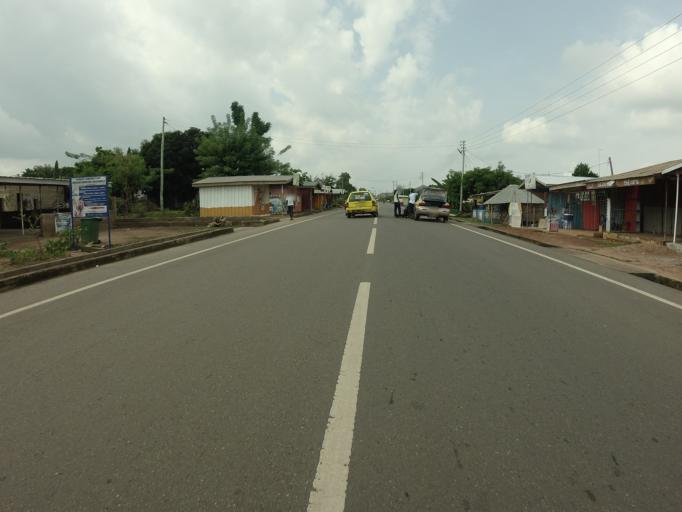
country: GH
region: Volta
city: Ho
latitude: 6.6264
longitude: 0.4863
